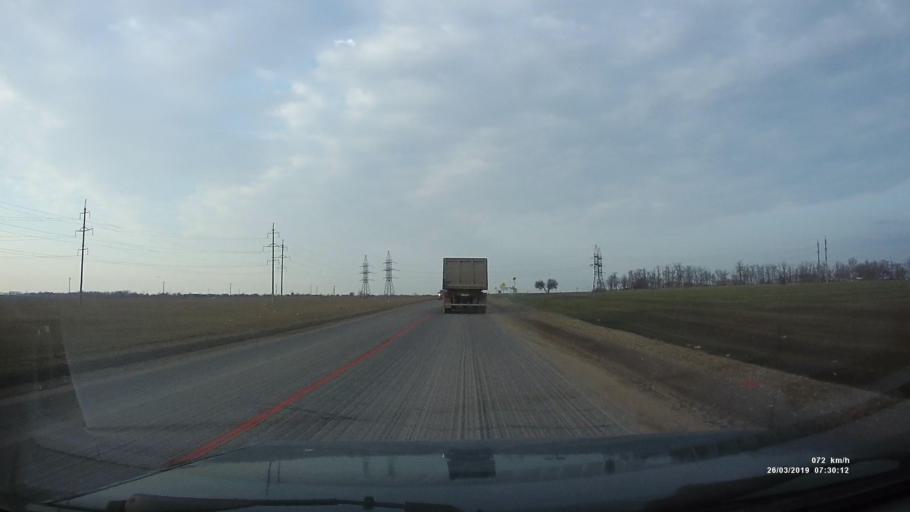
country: RU
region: Rostov
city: Novobessergenovka
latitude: 47.2384
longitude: 38.8094
